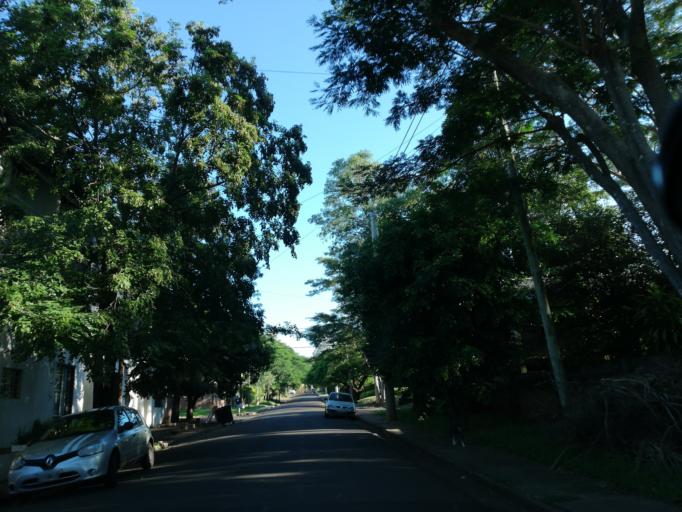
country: AR
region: Misiones
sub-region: Departamento de Capital
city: Posadas
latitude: -27.3561
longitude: -55.9207
